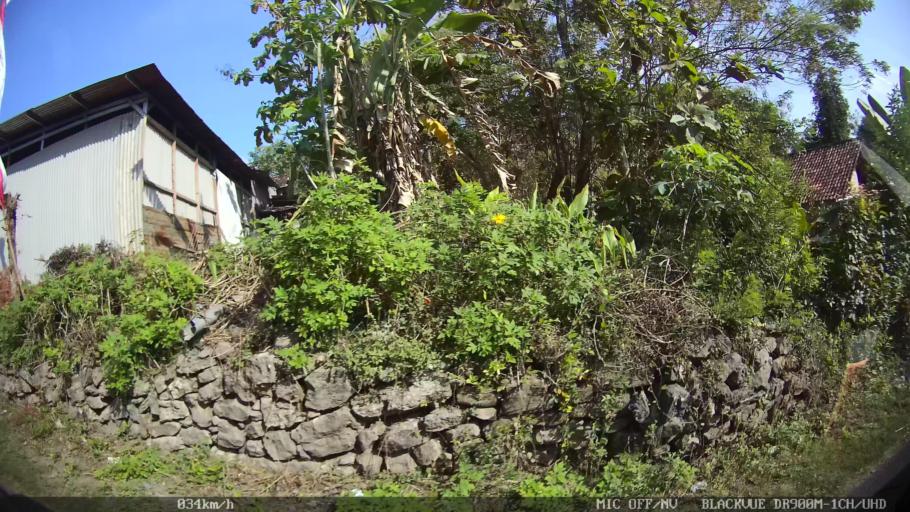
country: ID
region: Daerah Istimewa Yogyakarta
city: Kasihan
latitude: -7.8174
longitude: 110.2970
